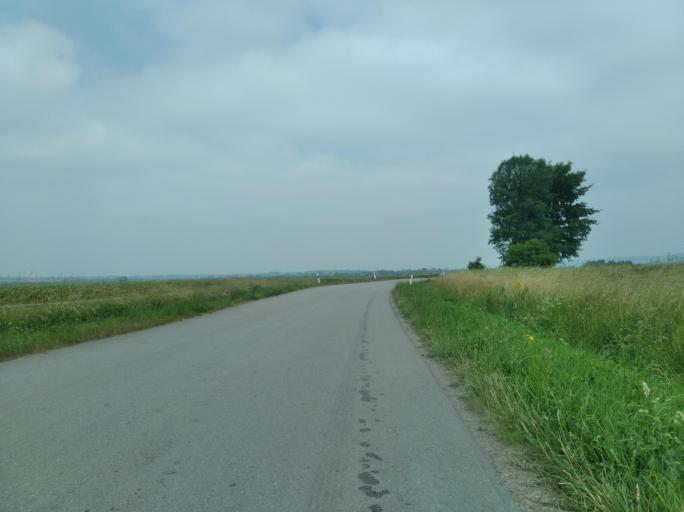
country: PL
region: Subcarpathian Voivodeship
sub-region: Powiat sanocki
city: Besko
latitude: 49.6003
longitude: 21.9572
